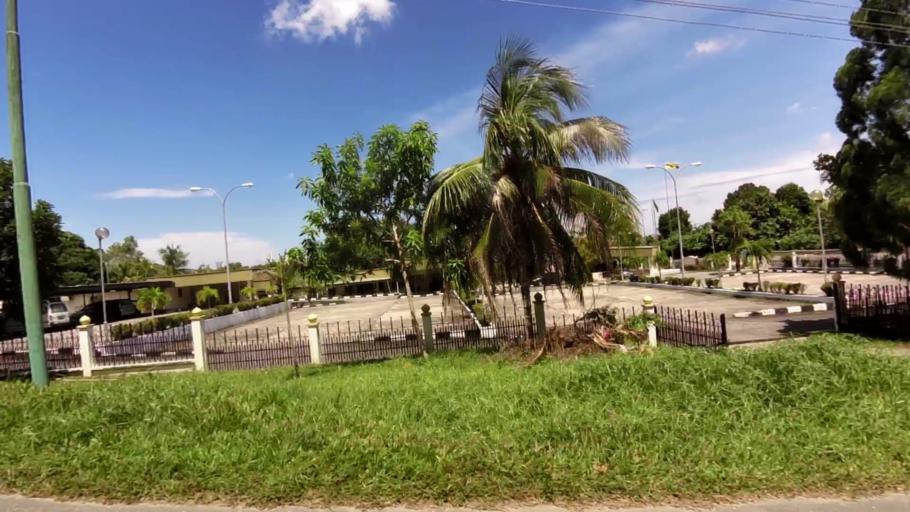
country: BN
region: Brunei and Muara
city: Bandar Seri Begawan
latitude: 4.9334
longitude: 114.9523
